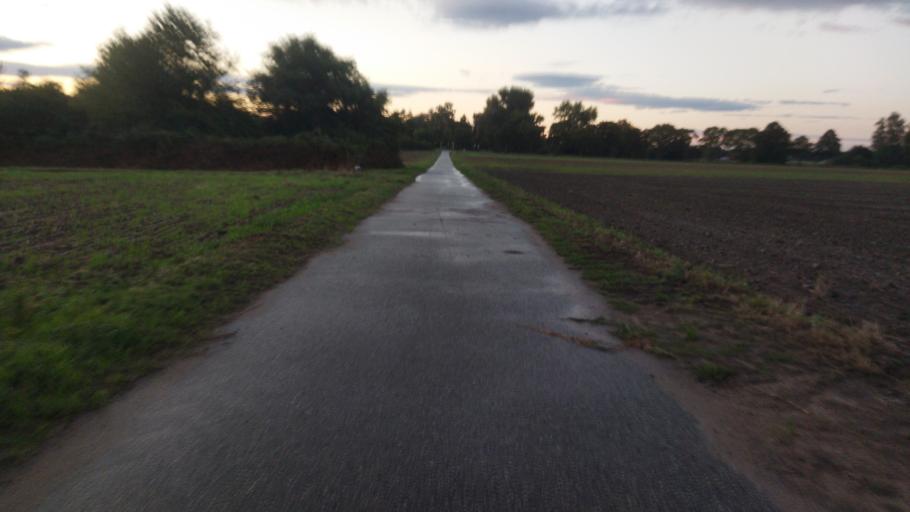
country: DE
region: Hesse
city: Lorsch
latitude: 49.6408
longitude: 8.5763
